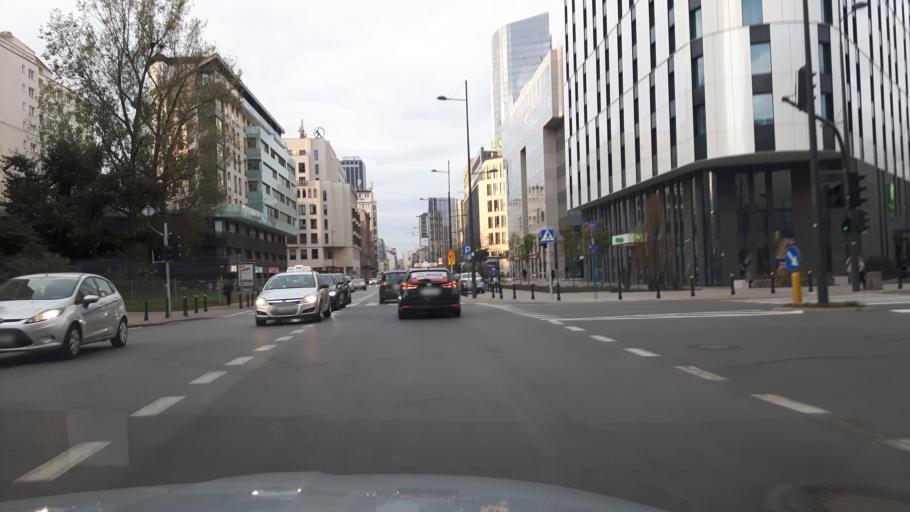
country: PL
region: Masovian Voivodeship
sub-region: Warszawa
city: Ochota
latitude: 52.2290
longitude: 20.9944
